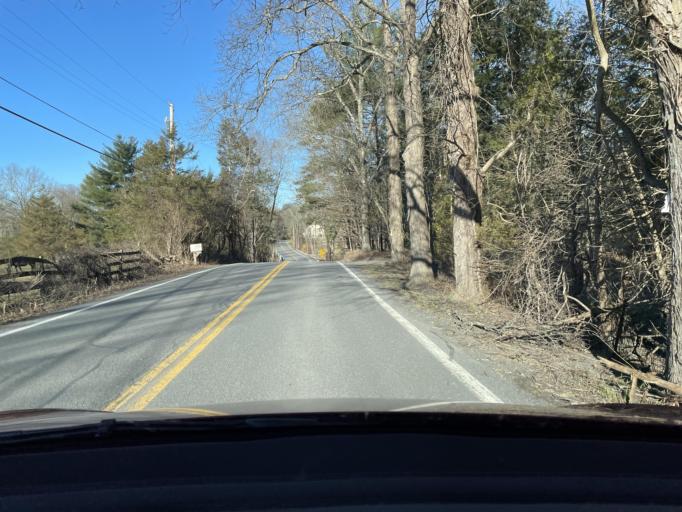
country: US
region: New York
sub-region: Ulster County
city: Zena
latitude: 42.0462
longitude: -74.0431
